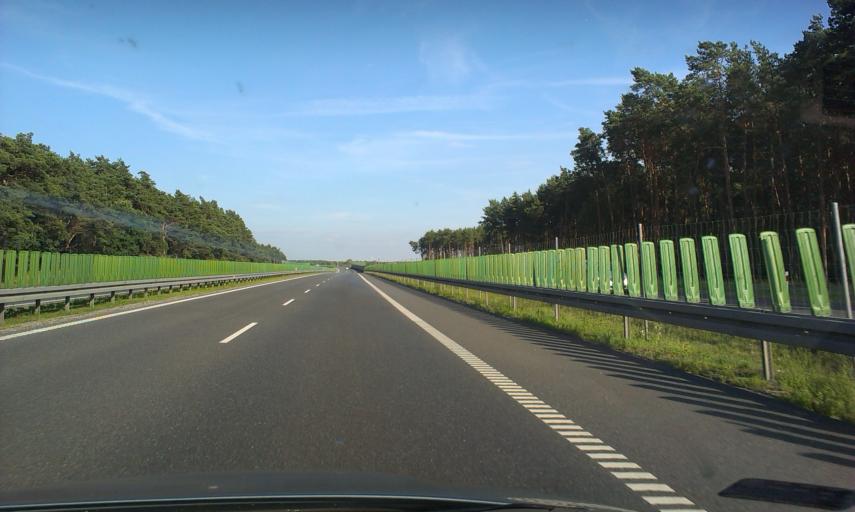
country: PL
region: Kujawsko-Pomorskie
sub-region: Powiat bydgoski
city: Biale Blota
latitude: 53.0617
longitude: 17.9537
